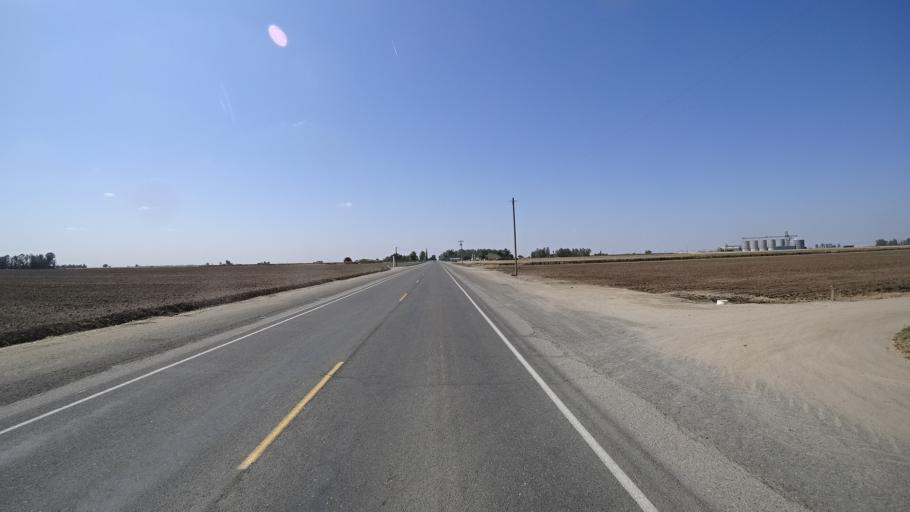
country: US
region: California
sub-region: Kings County
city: Home Garden
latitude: 36.2234
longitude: -119.6369
